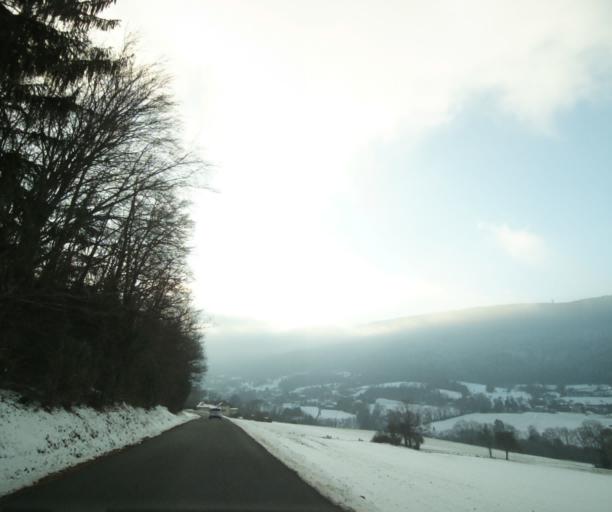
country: FR
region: Rhone-Alpes
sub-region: Departement de la Haute-Savoie
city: Monnetier-Mornex
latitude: 46.1390
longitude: 6.2263
